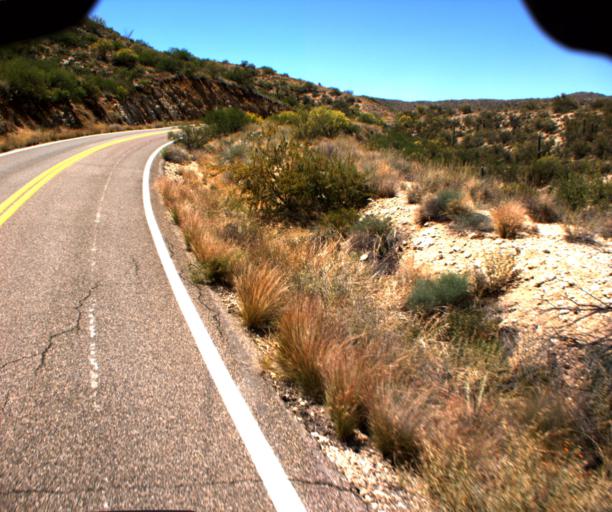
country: US
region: Arizona
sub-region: Yavapai County
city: Bagdad
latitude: 34.5188
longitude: -113.0954
